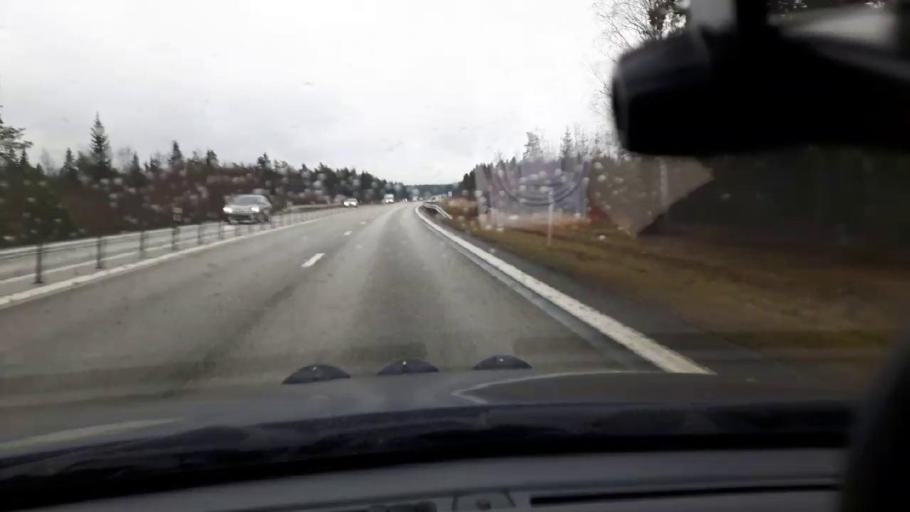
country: SE
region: Jaemtland
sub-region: OEstersunds Kommun
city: Brunflo
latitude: 63.1430
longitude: 14.7827
